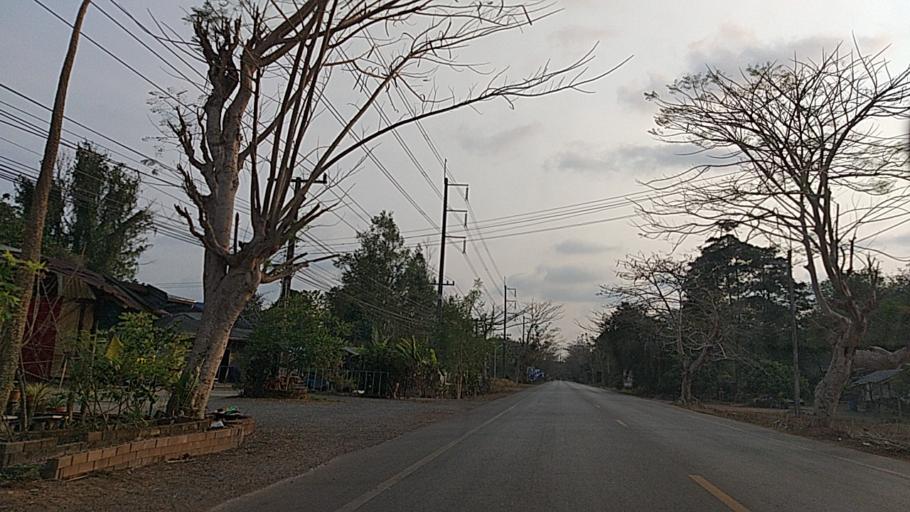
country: TH
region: Trat
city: Khao Saming
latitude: 12.2952
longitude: 102.3335
